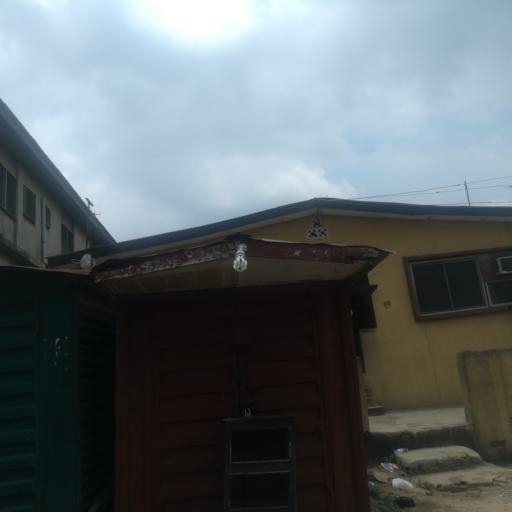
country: NG
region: Lagos
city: Ojota
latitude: 6.5843
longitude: 3.3834
